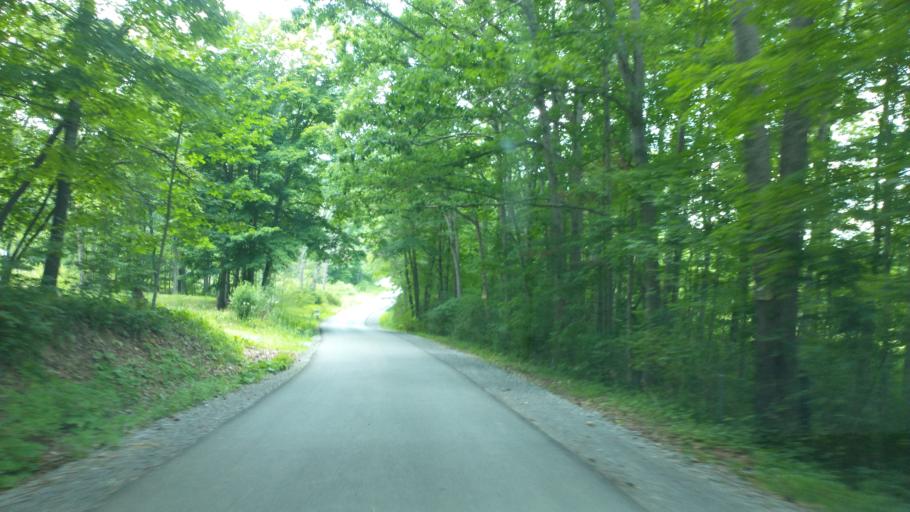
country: US
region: West Virginia
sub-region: Mercer County
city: Athens
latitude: 37.4536
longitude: -81.0615
